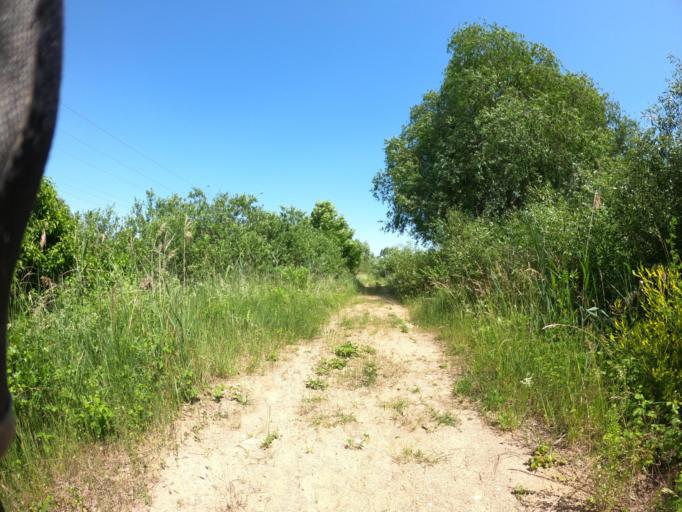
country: PL
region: West Pomeranian Voivodeship
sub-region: Powiat mysliborski
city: Mysliborz
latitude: 52.9125
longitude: 14.8459
